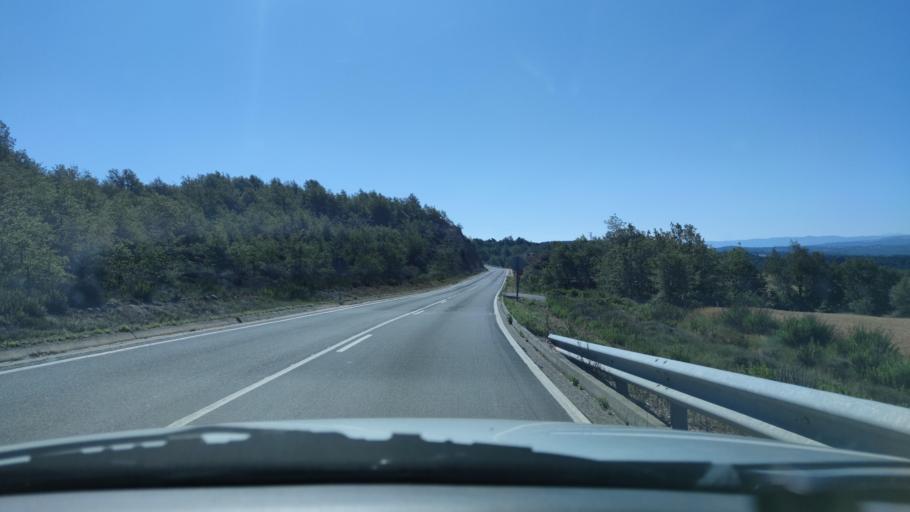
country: ES
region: Catalonia
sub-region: Provincia de Lleida
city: Solsona
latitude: 41.9097
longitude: 1.5241
